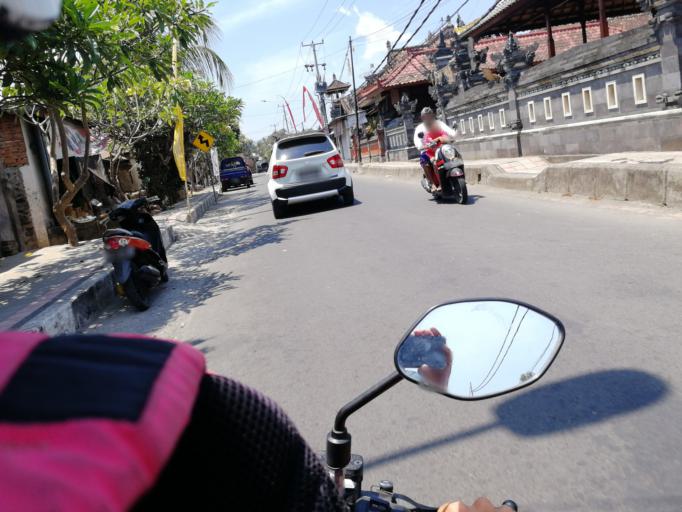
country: ID
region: Bali
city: Banjar Timbrah
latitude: -8.4786
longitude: 115.5972
